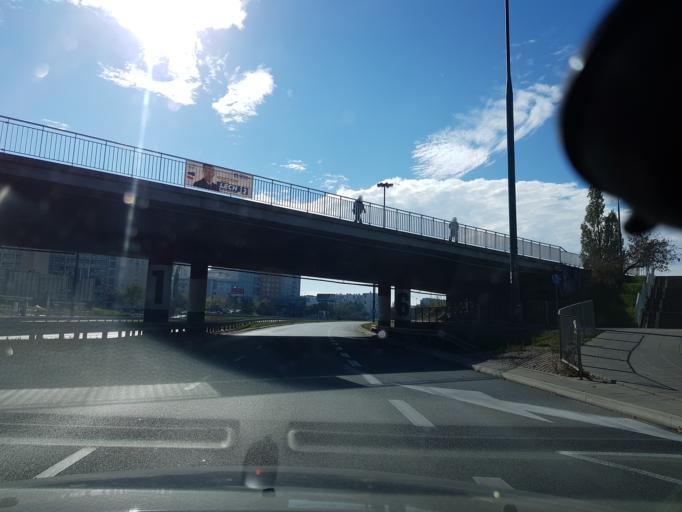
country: PL
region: Masovian Voivodeship
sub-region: Warszawa
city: Praga Poludnie
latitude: 52.2359
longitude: 21.0787
